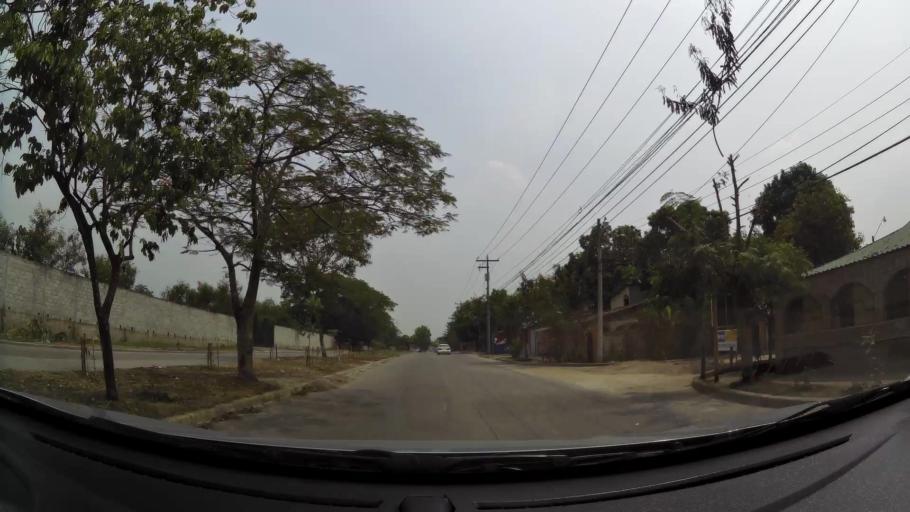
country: HN
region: Cortes
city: San Pedro Sula
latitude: 15.4781
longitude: -88.0260
